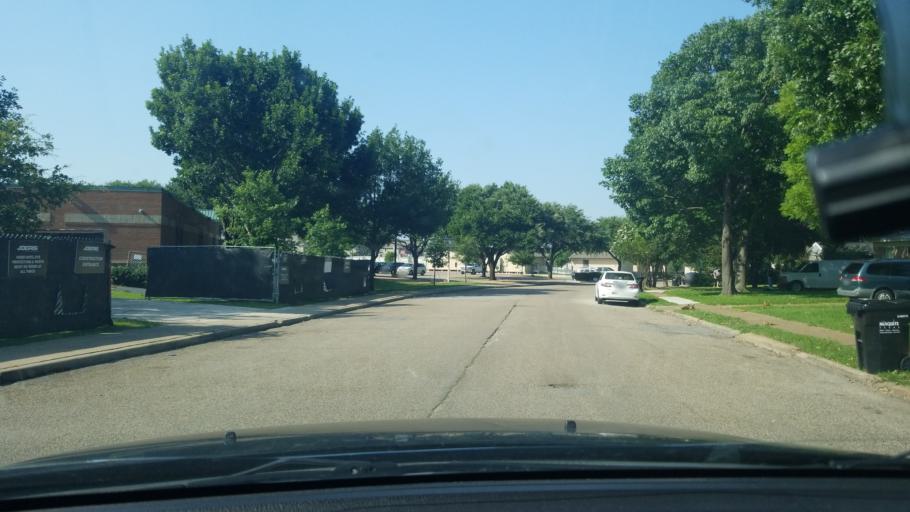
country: US
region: Texas
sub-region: Dallas County
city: Mesquite
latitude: 32.8286
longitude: -96.6463
